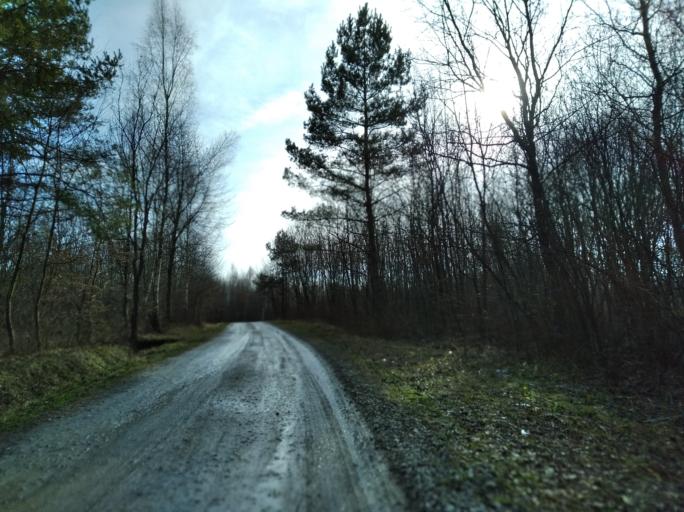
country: PL
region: Subcarpathian Voivodeship
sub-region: Powiat brzozowski
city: Grabownica Starzenska
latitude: 49.6437
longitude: 22.0643
